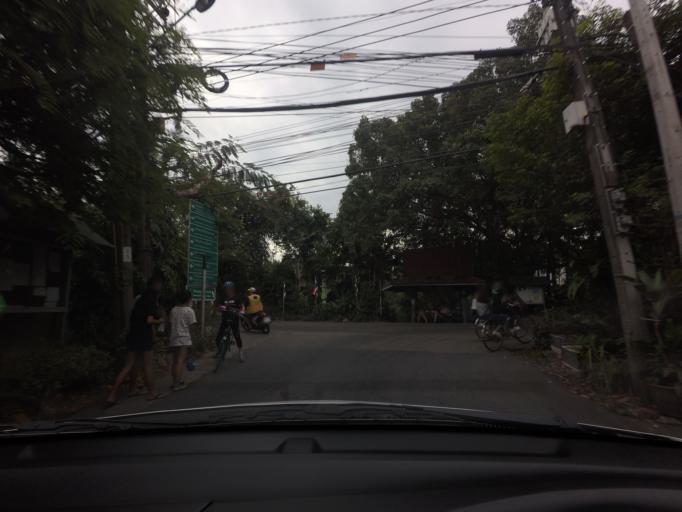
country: TH
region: Bangkok
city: Yan Nawa
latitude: 13.6861
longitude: 100.5688
